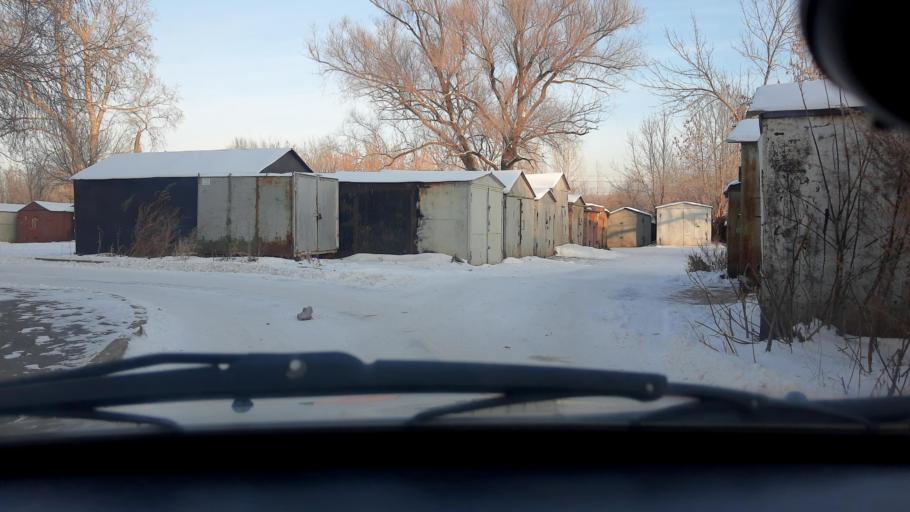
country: RU
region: Bashkortostan
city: Ufa
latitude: 54.8209
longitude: 56.1280
